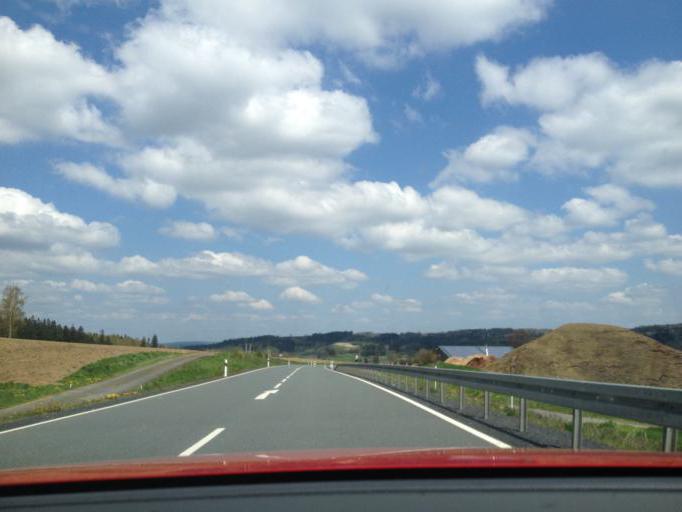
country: DE
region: Bavaria
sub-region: Upper Franconia
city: Marktredwitz
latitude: 49.9787
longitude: 12.1119
